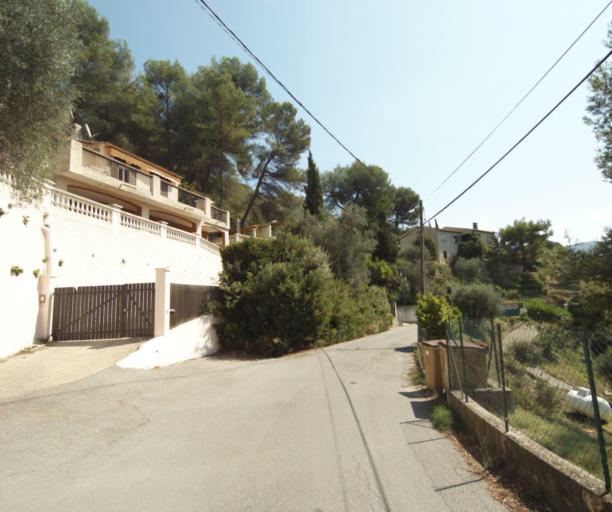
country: FR
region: Provence-Alpes-Cote d'Azur
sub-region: Departement des Alpes-Maritimes
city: Drap
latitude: 43.7583
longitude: 7.3242
